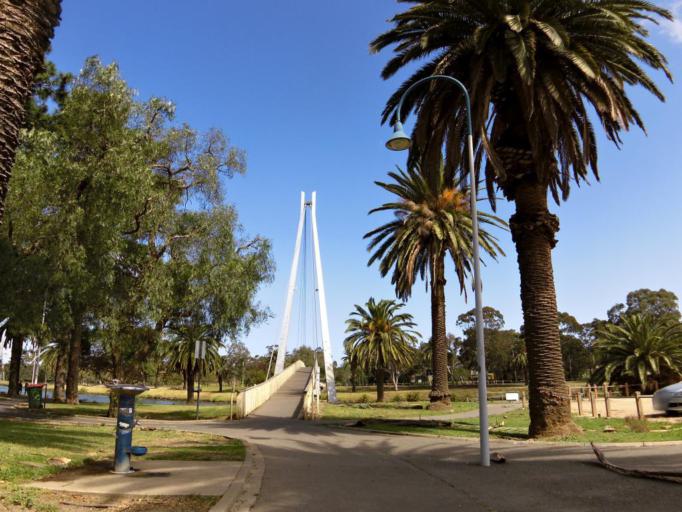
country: AU
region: Victoria
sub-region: Moonee Valley
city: Essendon West
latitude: -37.7612
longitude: 144.8892
